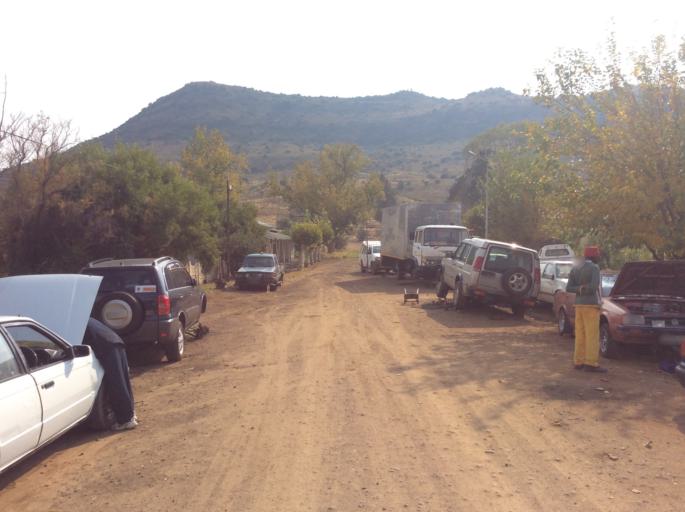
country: LS
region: Mafeteng
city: Mafeteng
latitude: -29.7252
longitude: 27.0433
